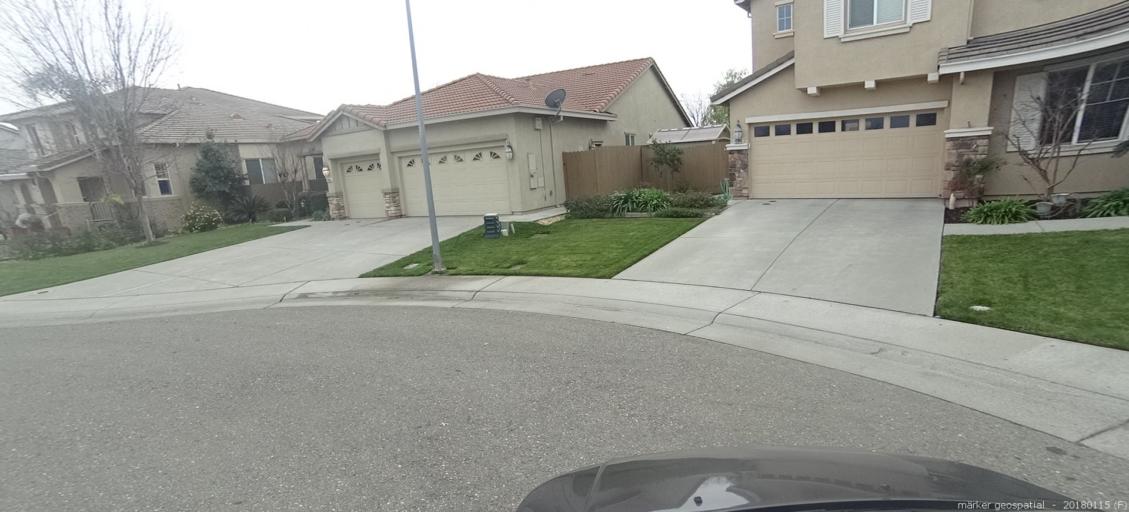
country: US
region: California
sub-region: Sacramento County
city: Rancho Cordova
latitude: 38.5803
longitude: -121.2820
